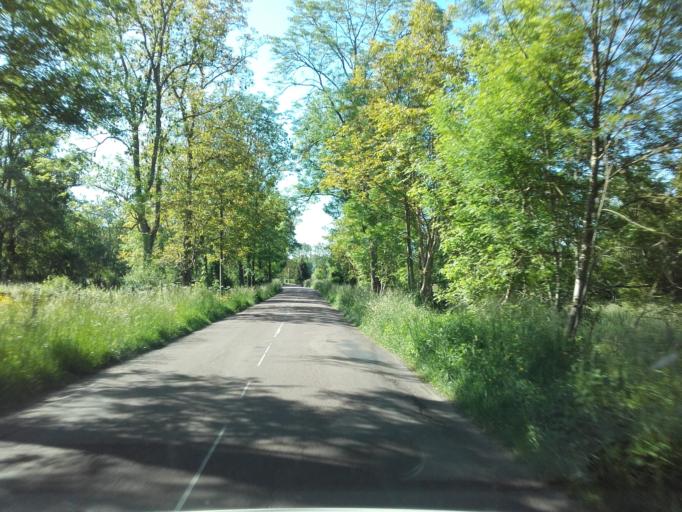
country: FR
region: Bourgogne
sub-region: Departement de la Cote-d'Or
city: Nolay
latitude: 46.9399
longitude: 4.6294
